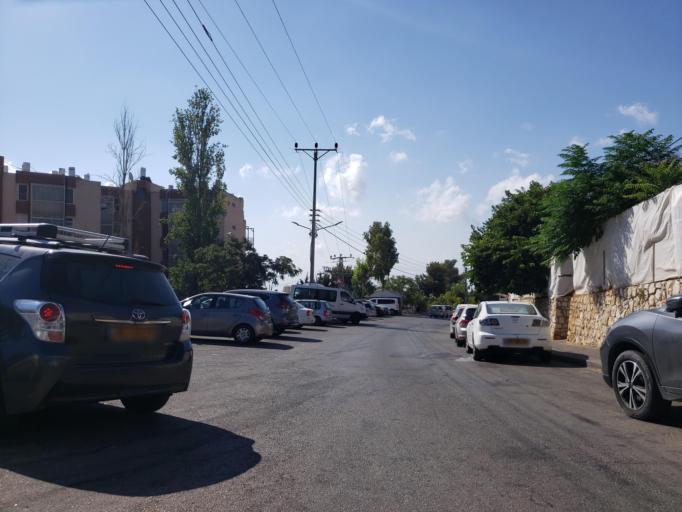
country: IL
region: Northern District
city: Safed
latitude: 32.9584
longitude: 35.5001
